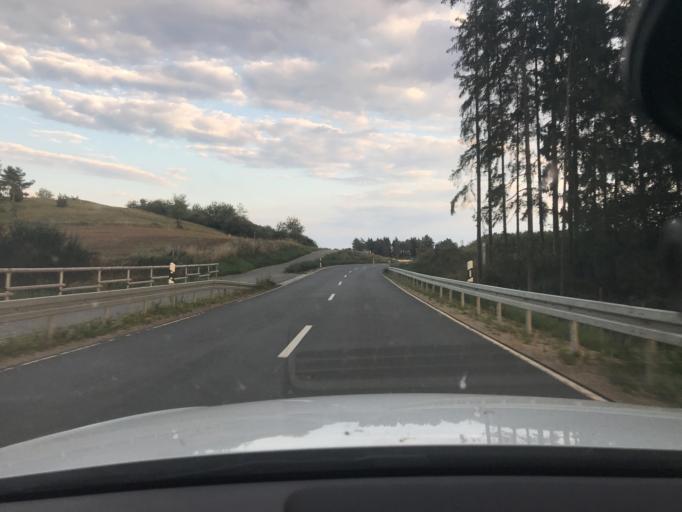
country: DE
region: Bavaria
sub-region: Upper Palatinate
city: Auerbach
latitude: 49.7261
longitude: 11.6141
